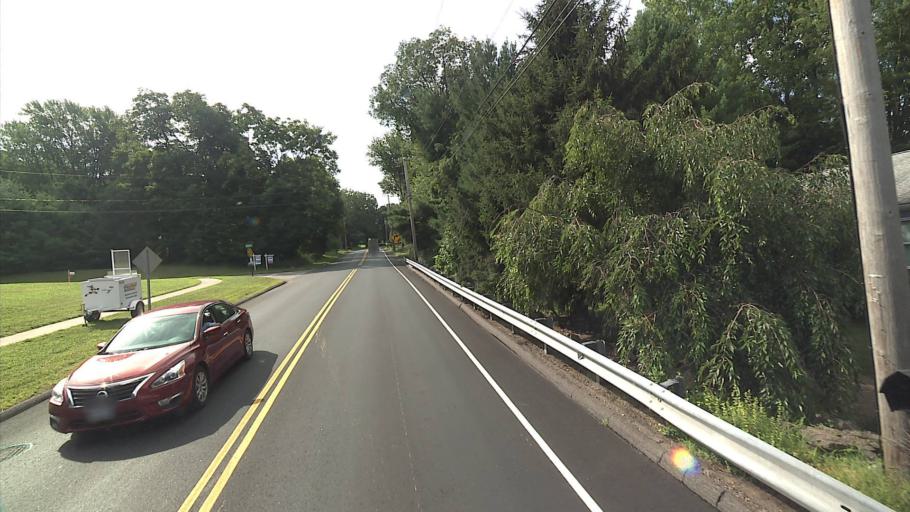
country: US
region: Connecticut
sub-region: New Haven County
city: Seymour
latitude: 41.3812
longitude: -73.0656
